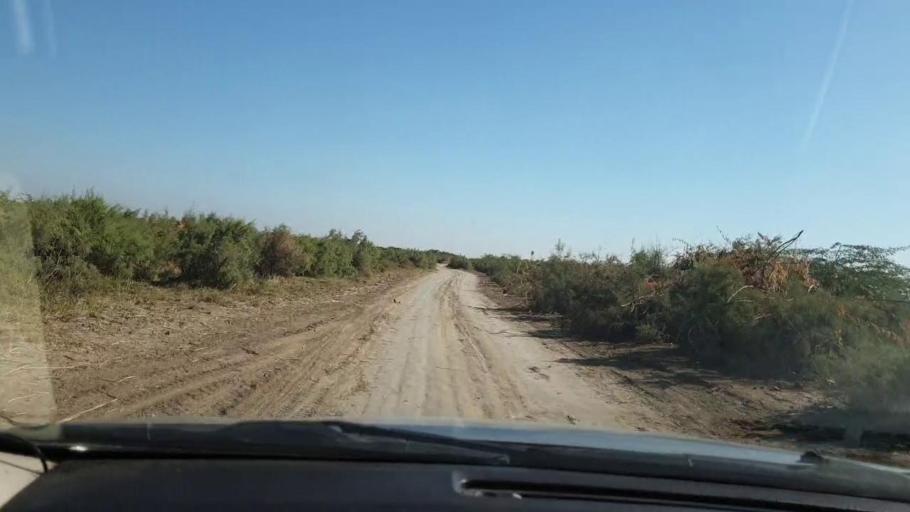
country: PK
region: Sindh
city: Berani
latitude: 25.7191
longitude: 68.9835
